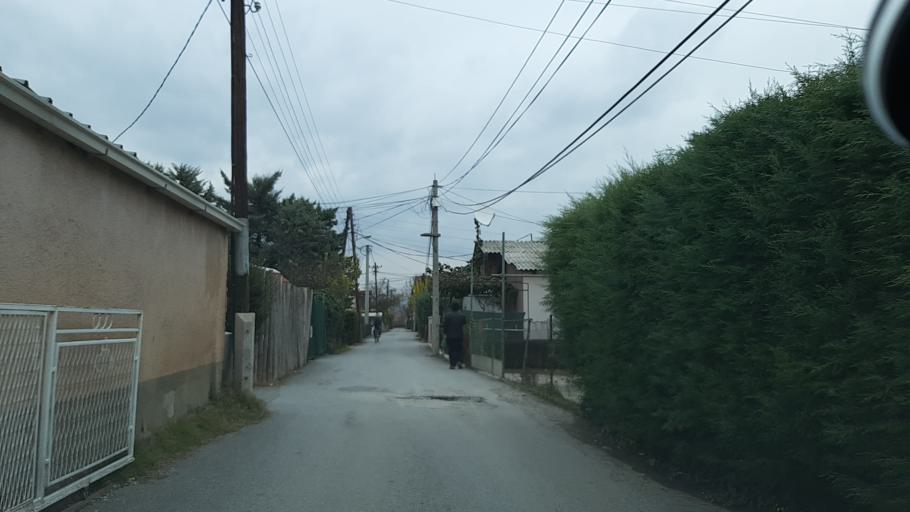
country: MK
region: Kisela Voda
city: Usje
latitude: 41.9783
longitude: 21.4787
